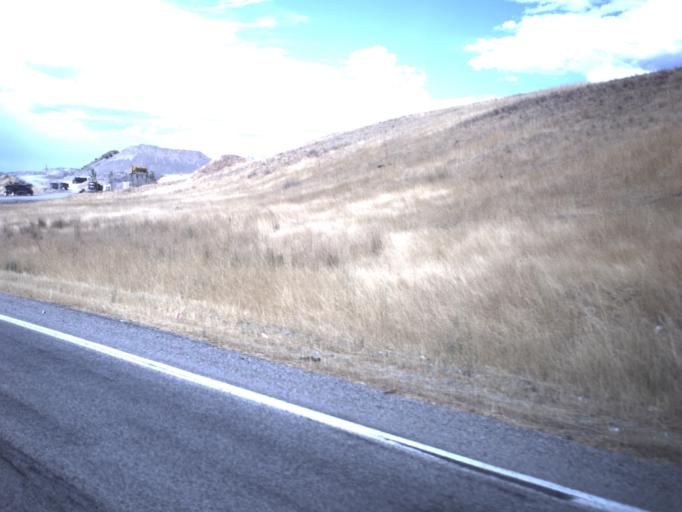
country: US
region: Utah
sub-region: Box Elder County
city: Garland
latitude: 41.7424
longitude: -112.0986
